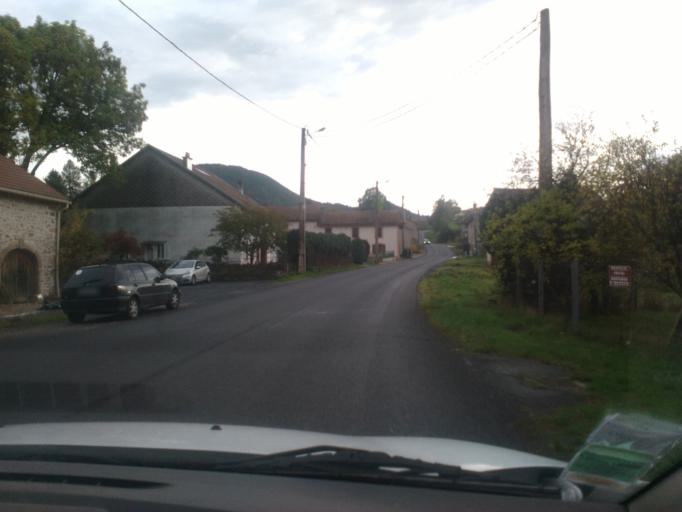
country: FR
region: Lorraine
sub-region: Departement des Vosges
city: Granges-sur-Vologne
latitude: 48.1811
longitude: 6.8068
